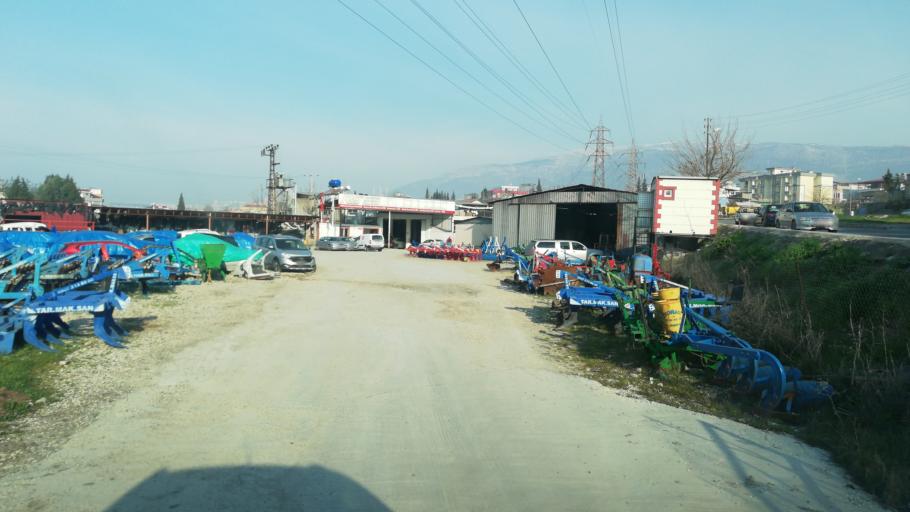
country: TR
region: Kahramanmaras
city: Kahramanmaras
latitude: 37.5643
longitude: 36.9454
